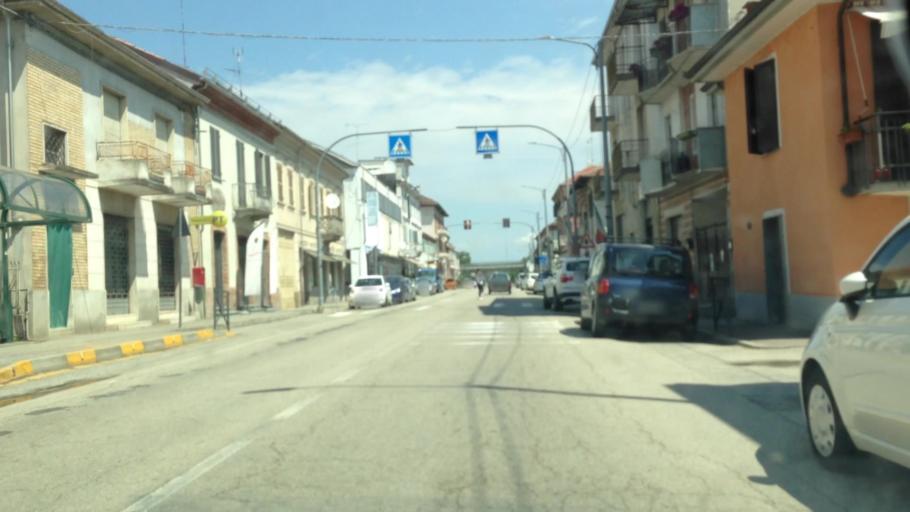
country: IT
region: Piedmont
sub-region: Provincia di Asti
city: Castell'Alfero
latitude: 44.9569
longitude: 8.2234
